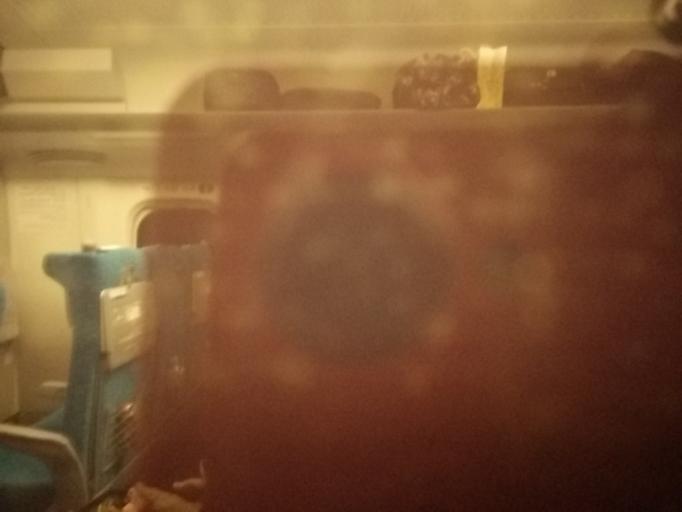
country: JP
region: Kanagawa
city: Yokohama
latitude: 35.5252
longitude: 139.6351
